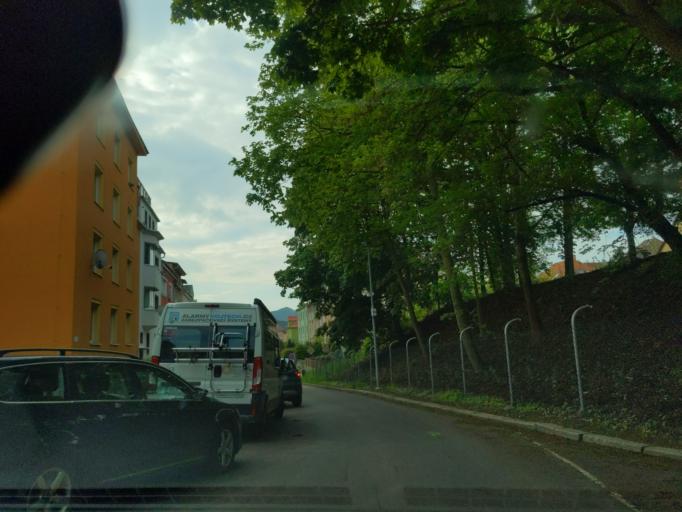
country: CZ
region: Ustecky
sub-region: Okres Usti nad Labem
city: Usti nad Labem
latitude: 50.6733
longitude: 14.0171
